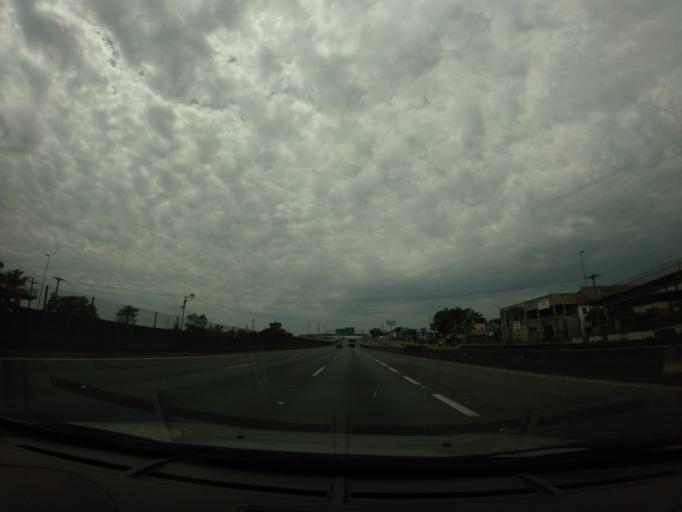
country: BR
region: Sao Paulo
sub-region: Hortolandia
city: Hortolandia
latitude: -22.8251
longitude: -47.1886
